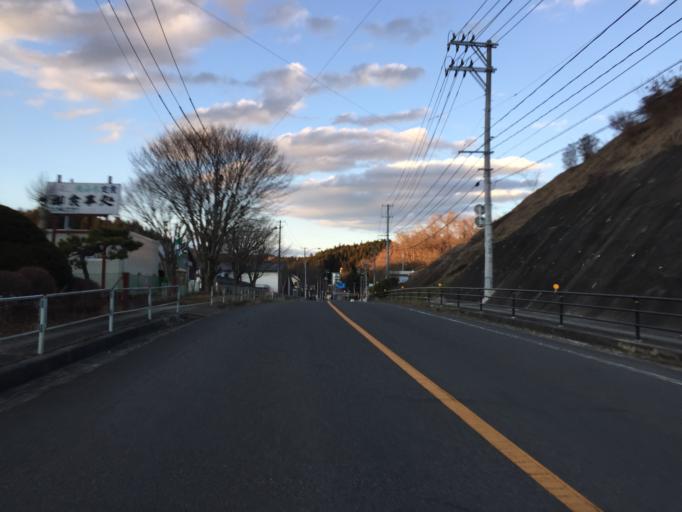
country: JP
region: Fukushima
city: Funehikimachi-funehiki
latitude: 37.2840
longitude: 140.6343
